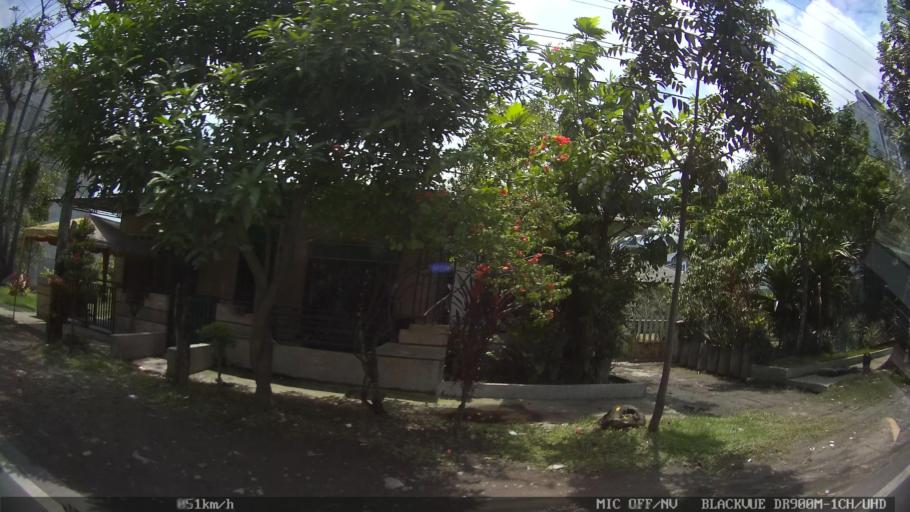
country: ID
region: North Sumatra
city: Medan
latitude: 3.6156
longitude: 98.7032
